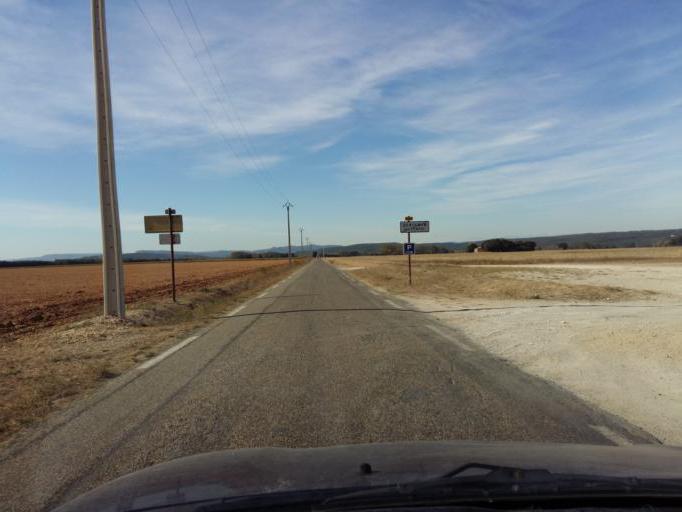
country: FR
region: Provence-Alpes-Cote d'Azur
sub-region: Departement du Vaucluse
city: Serignan-du-Comtat
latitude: 44.1883
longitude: 4.8346
